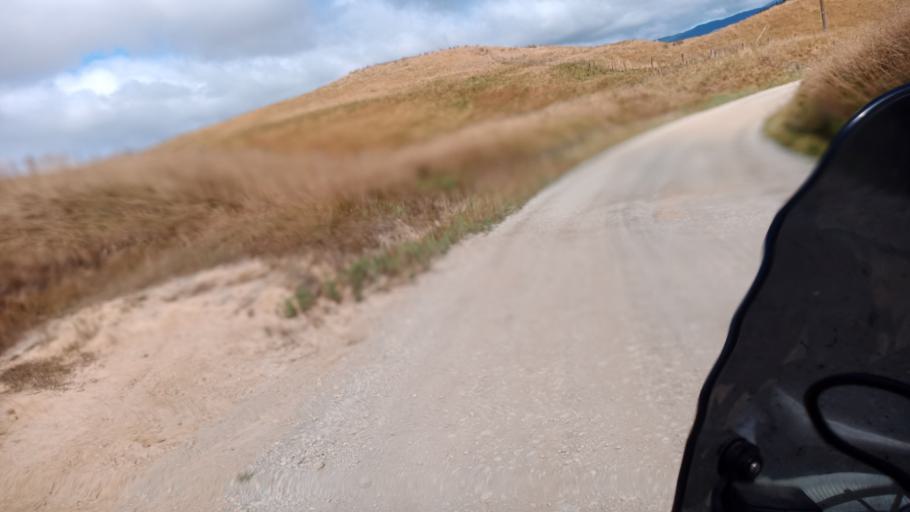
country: NZ
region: Hawke's Bay
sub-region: Wairoa District
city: Wairoa
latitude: -38.6092
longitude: 177.4616
